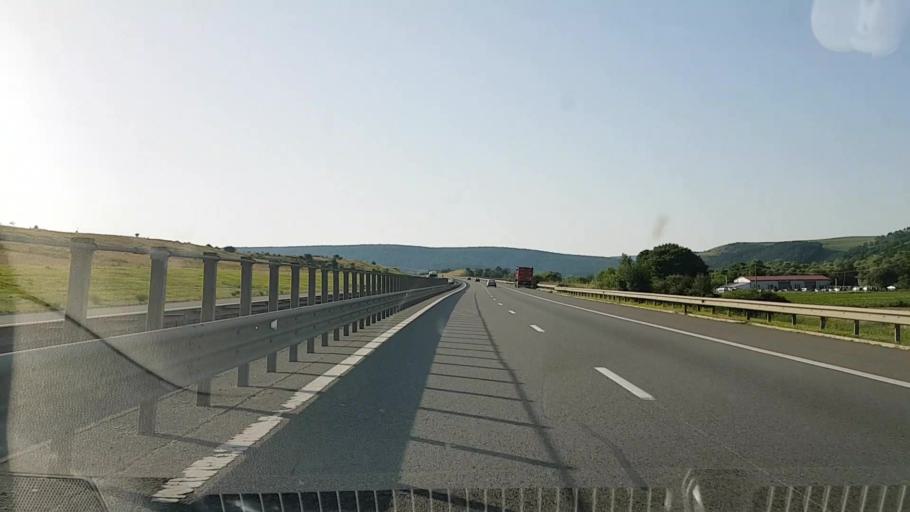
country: RO
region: Cluj
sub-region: Comuna Savadisla
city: Savadisla
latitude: 46.7046
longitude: 23.4314
